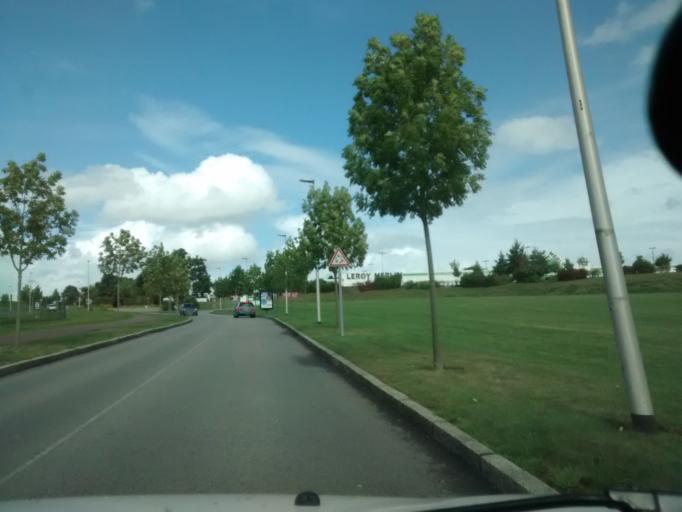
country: FR
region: Brittany
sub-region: Departement d'Ille-et-Vilaine
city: Betton
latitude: 48.1622
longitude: -1.6353
